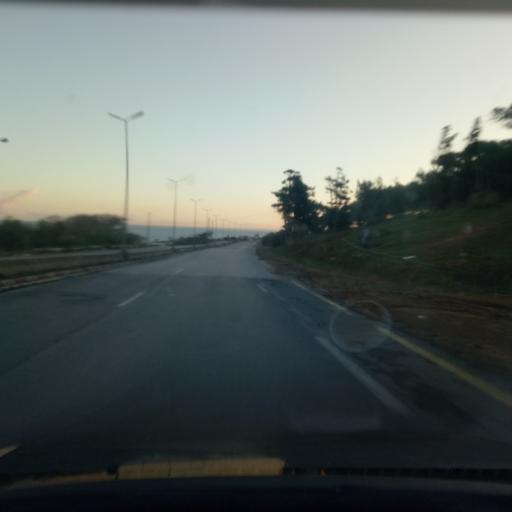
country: DZ
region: Tipaza
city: Bou Ismail
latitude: 36.6568
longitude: 2.7201
